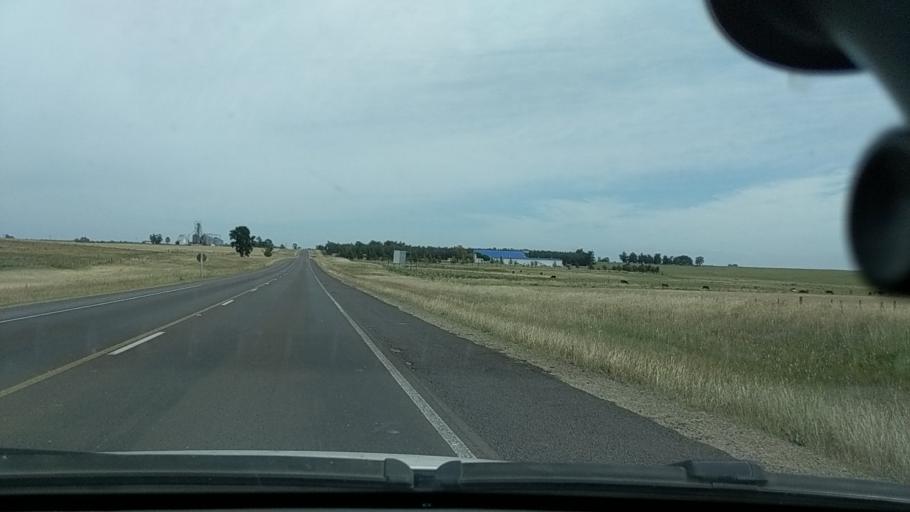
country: UY
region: Durazno
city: Durazno
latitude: -33.4573
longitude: -56.4666
